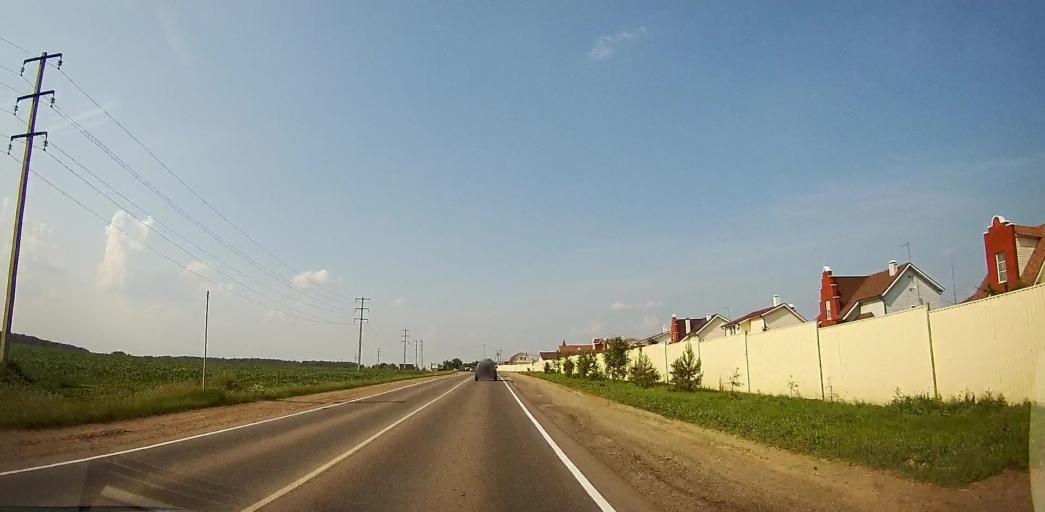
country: RU
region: Moskovskaya
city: Barybino
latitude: 55.2952
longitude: 37.9123
